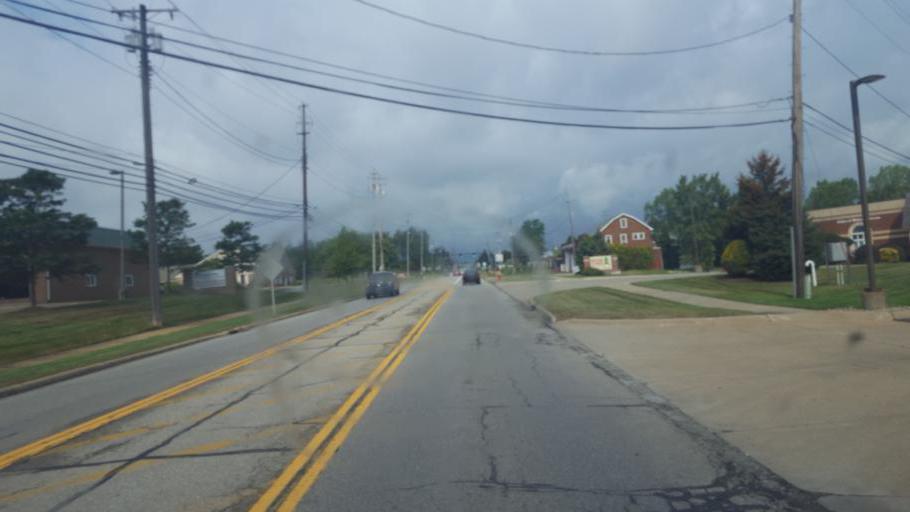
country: US
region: Ohio
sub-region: Geauga County
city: Chardon
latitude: 41.5841
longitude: -81.2142
